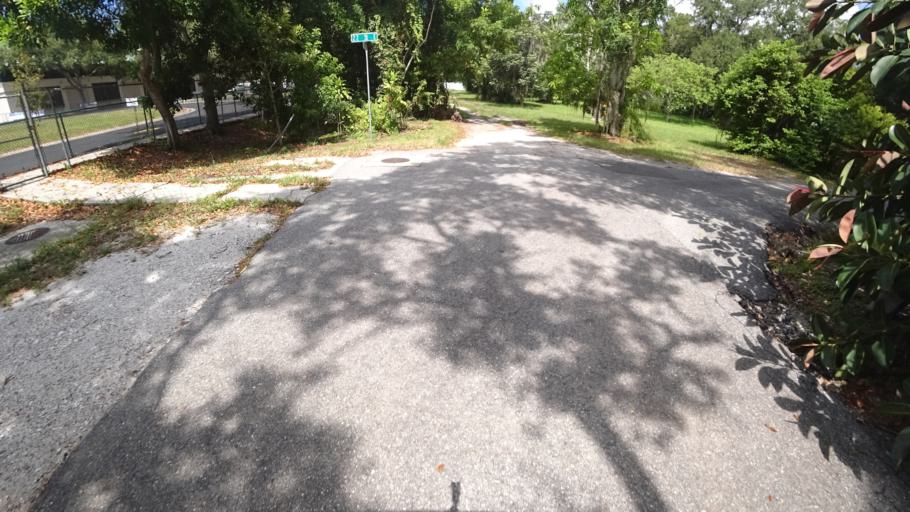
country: US
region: Florida
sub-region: Manatee County
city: Samoset
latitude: 27.4493
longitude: -82.5372
